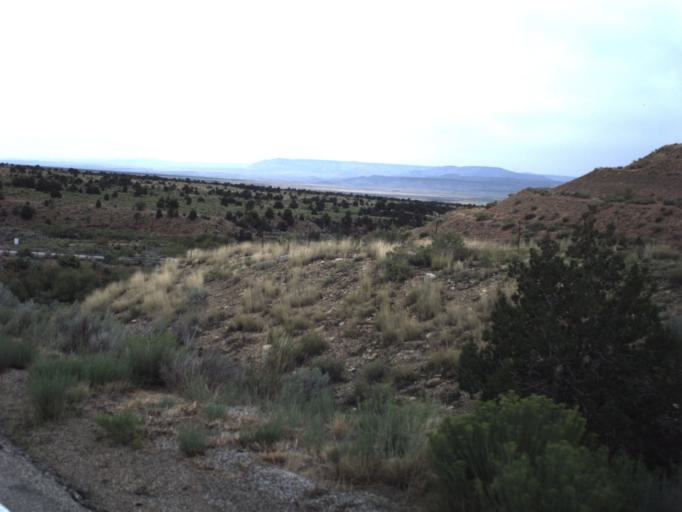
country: US
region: Utah
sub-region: Carbon County
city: East Carbon City
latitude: 39.5415
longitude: -110.4063
